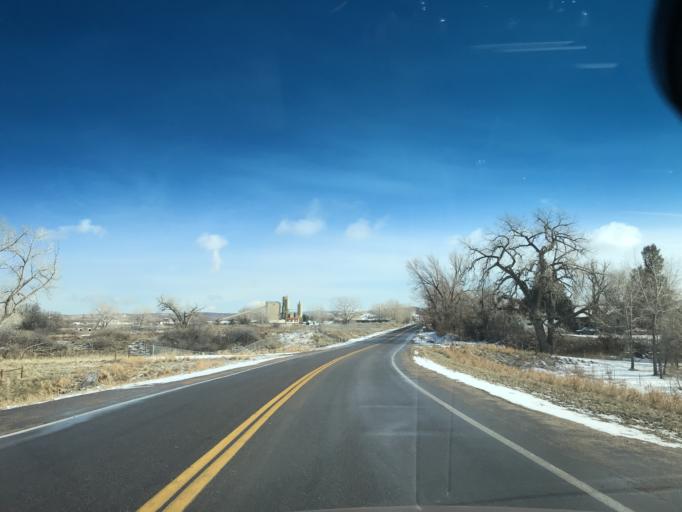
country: US
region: Colorado
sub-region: Douglas County
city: Roxborough Park
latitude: 39.4710
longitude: -104.9979
